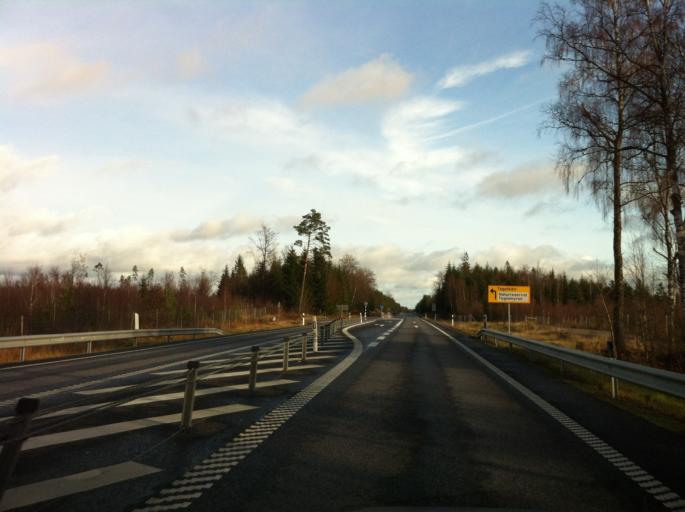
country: SE
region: Kronoberg
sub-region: Alvesta Kommun
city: Vislanda
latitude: 56.6880
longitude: 14.3241
